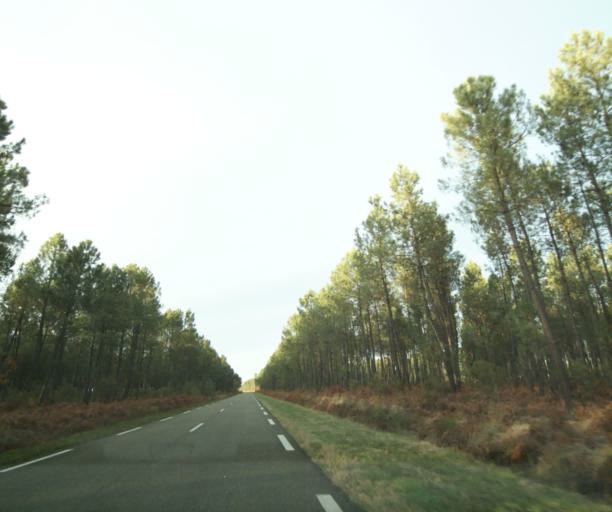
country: FR
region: Aquitaine
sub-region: Departement des Landes
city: Roquefort
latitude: 44.1643
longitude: -0.1358
